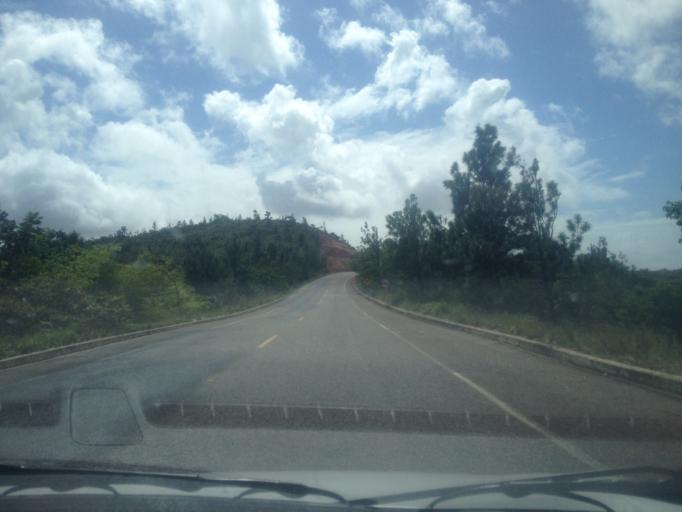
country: BR
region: Bahia
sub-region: Conde
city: Conde
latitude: -11.9857
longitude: -37.6776
